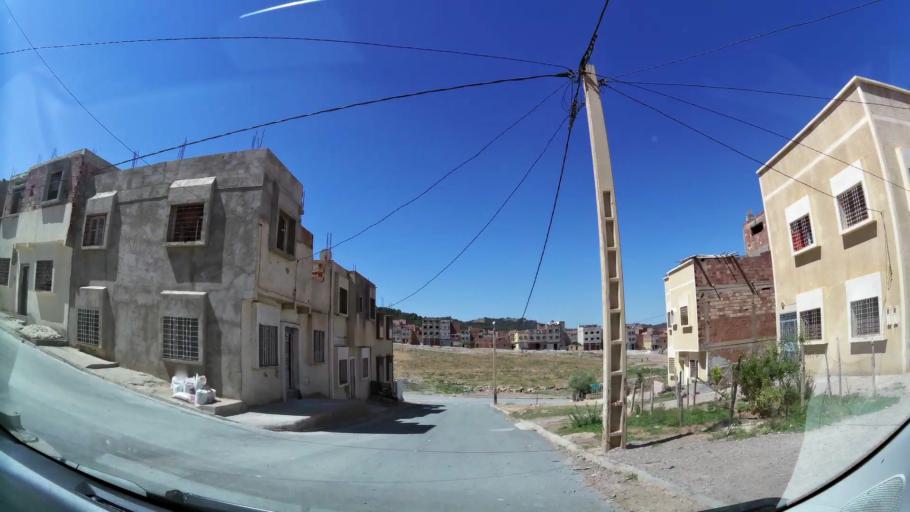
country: MA
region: Oriental
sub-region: Oujda-Angad
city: Oujda
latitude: 34.6518
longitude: -1.8718
